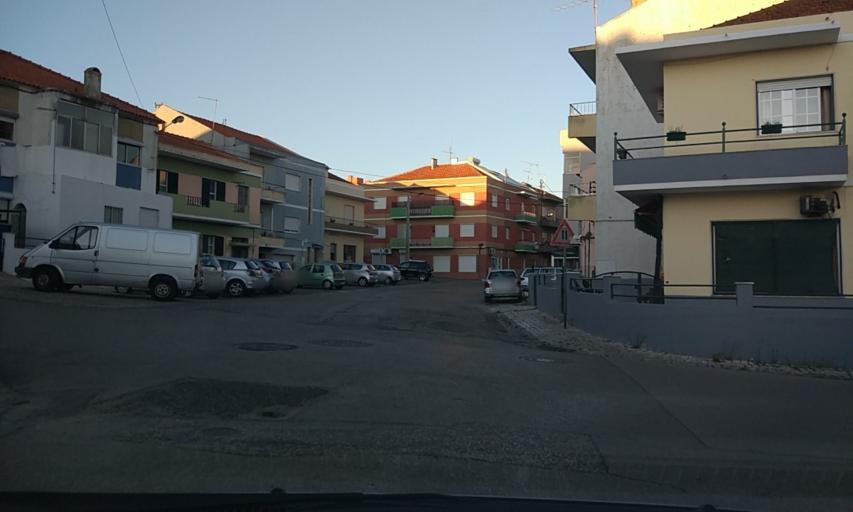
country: PT
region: Setubal
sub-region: Setubal
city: Setubal
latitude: 38.5388
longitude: -8.8798
